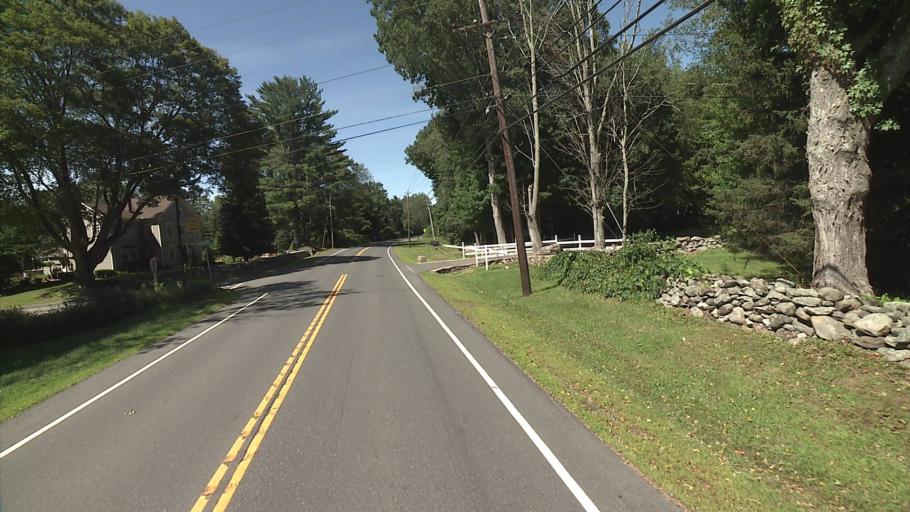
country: US
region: Connecticut
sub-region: New Haven County
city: Oxford
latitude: 41.4234
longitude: -73.1545
